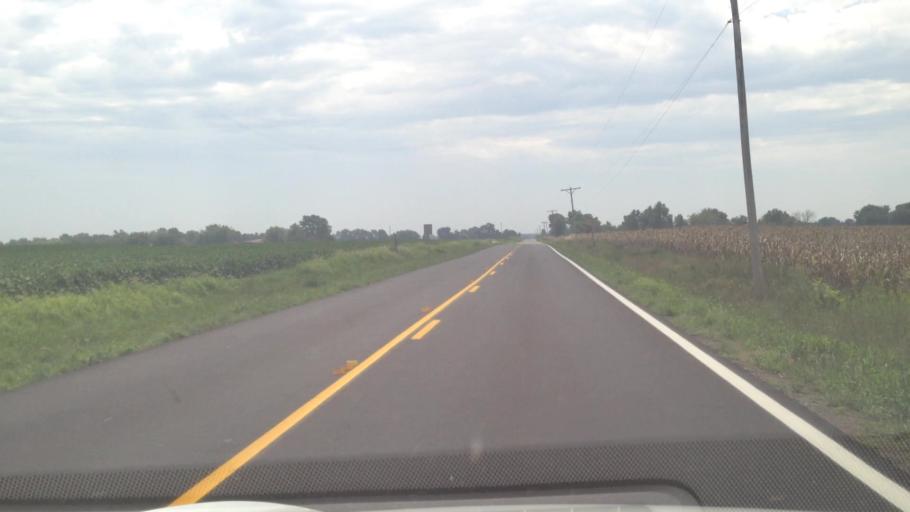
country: US
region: Kansas
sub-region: Crawford County
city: Girard
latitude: 37.6339
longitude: -94.9698
